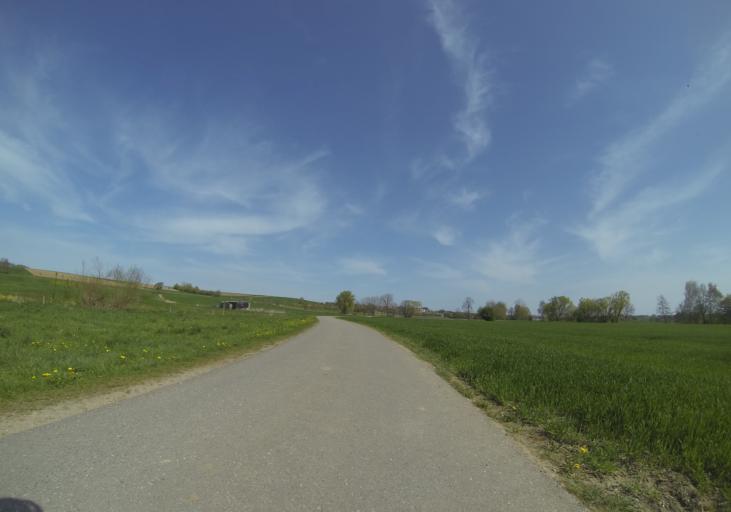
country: DE
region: Baden-Wuerttemberg
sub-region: Tuebingen Region
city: Achstetten
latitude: 48.2470
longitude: 9.9130
